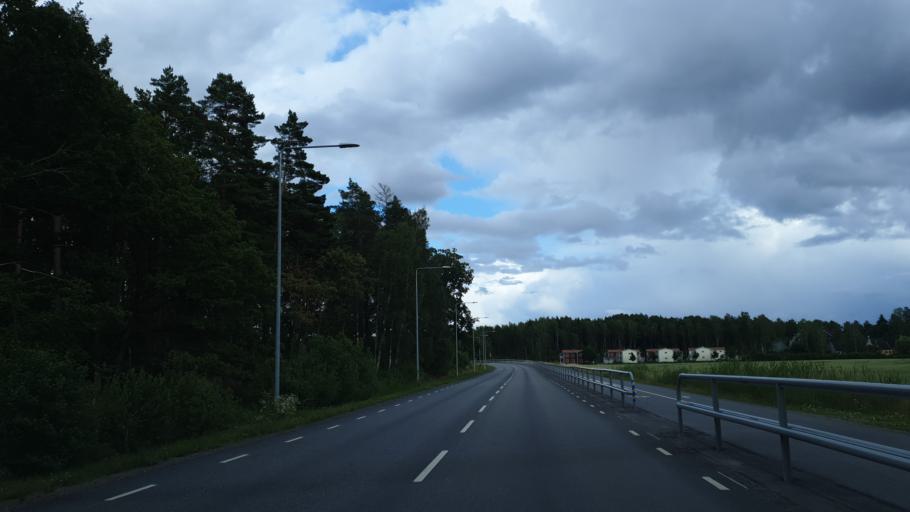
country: SE
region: Stockholm
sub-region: Jarfalla Kommun
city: Jakobsberg
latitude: 59.4252
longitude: 17.7996
